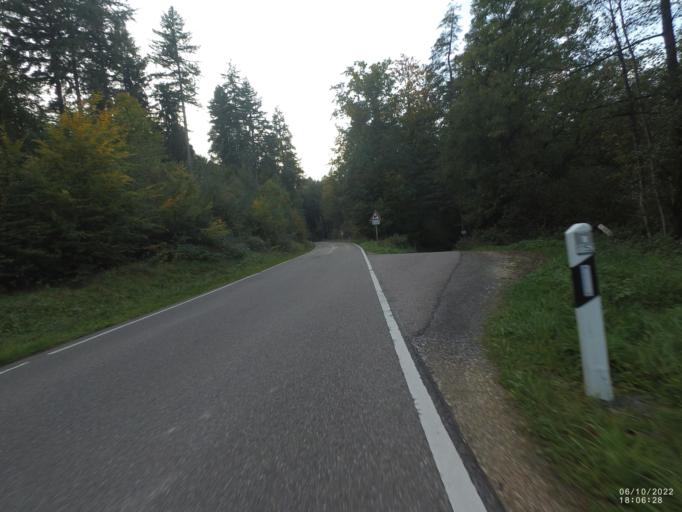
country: DE
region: Baden-Wuerttemberg
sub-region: Regierungsbezirk Stuttgart
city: Ebersbach an der Fils
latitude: 48.7579
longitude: 9.5055
